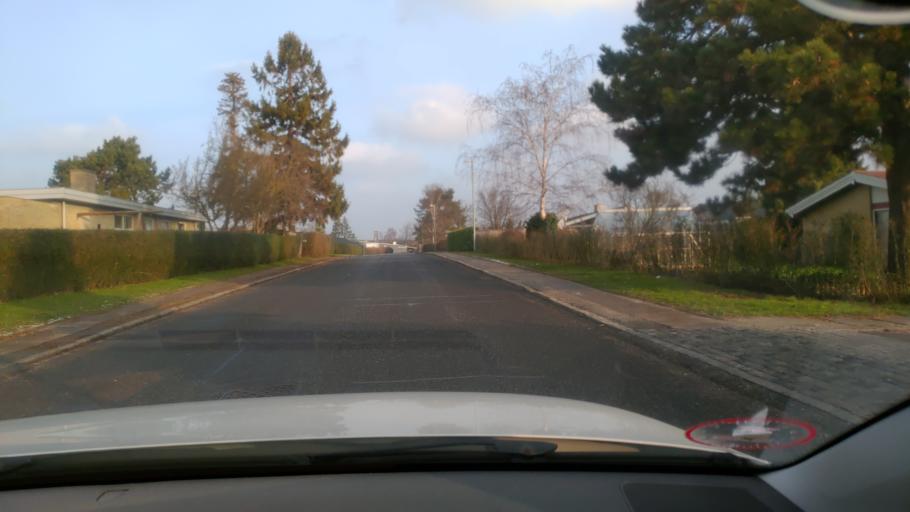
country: DK
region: Zealand
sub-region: Solrod Kommune
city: Solrod Strand
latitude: 55.5370
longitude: 12.2133
